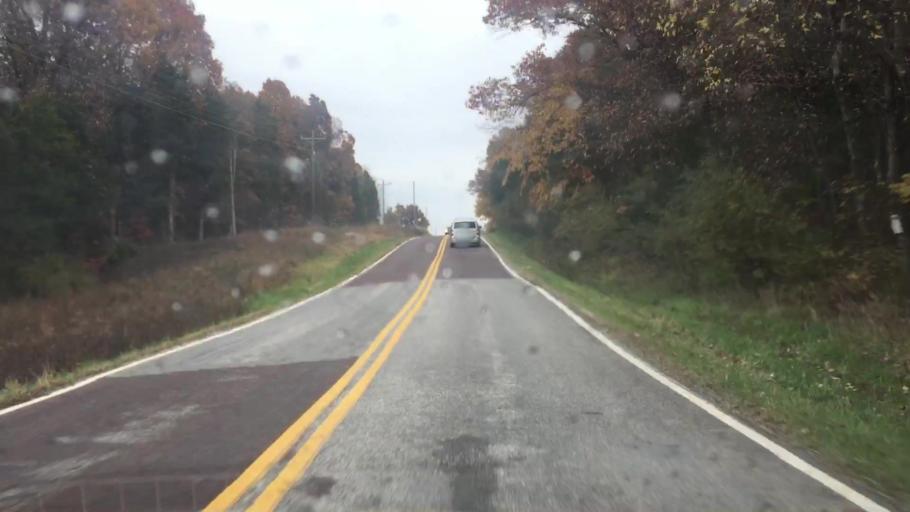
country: US
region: Missouri
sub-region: Callaway County
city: Fulton
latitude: 38.7877
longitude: -91.7754
